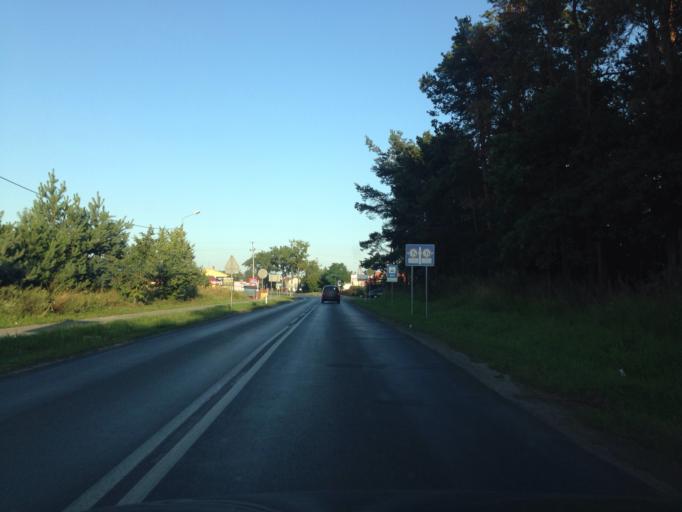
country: PL
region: Kujawsko-Pomorskie
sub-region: Powiat aleksandrowski
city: Aleksandrow Kujawski
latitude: 52.8650
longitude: 18.7196
